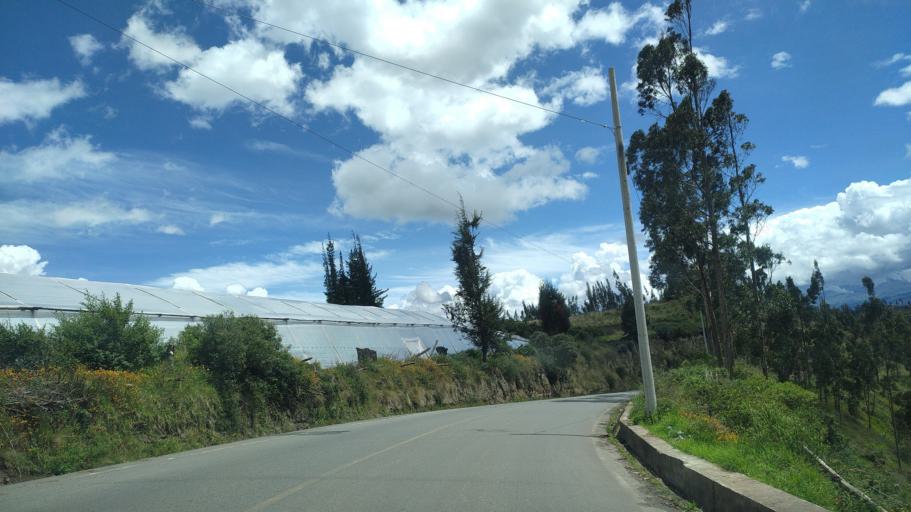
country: EC
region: Chimborazo
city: Riobamba
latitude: -1.6624
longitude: -78.5799
